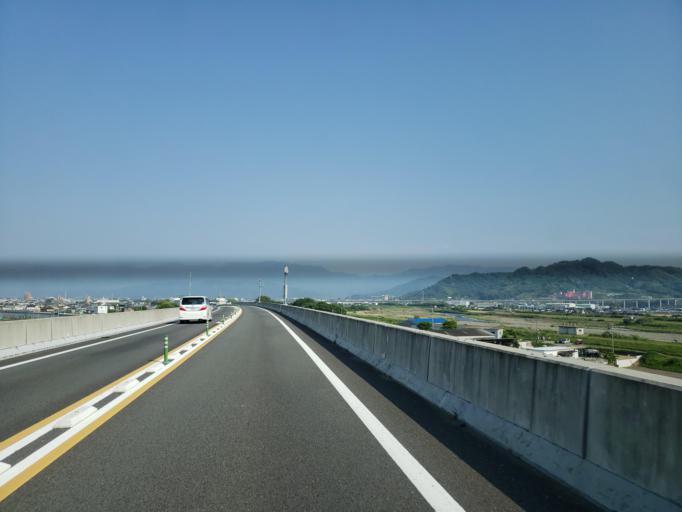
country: JP
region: Ehime
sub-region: Shikoku-chuo Shi
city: Matsuyama
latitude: 33.8037
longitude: 132.7615
